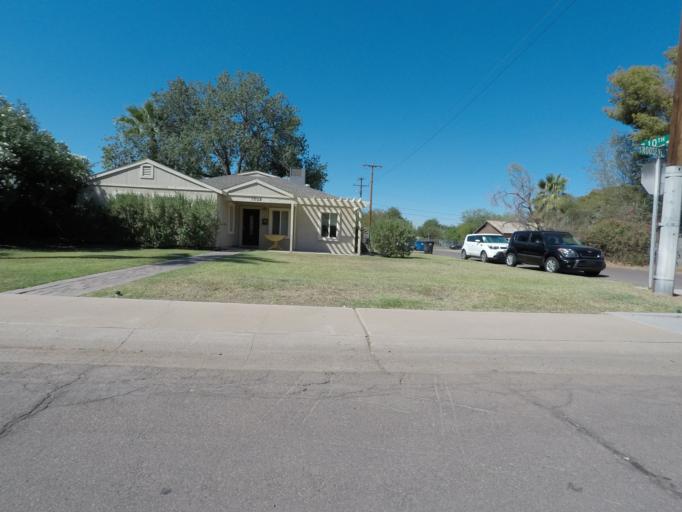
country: US
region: Arizona
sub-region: Maricopa County
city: Tempe Junction
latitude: 33.4193
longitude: -111.9473
